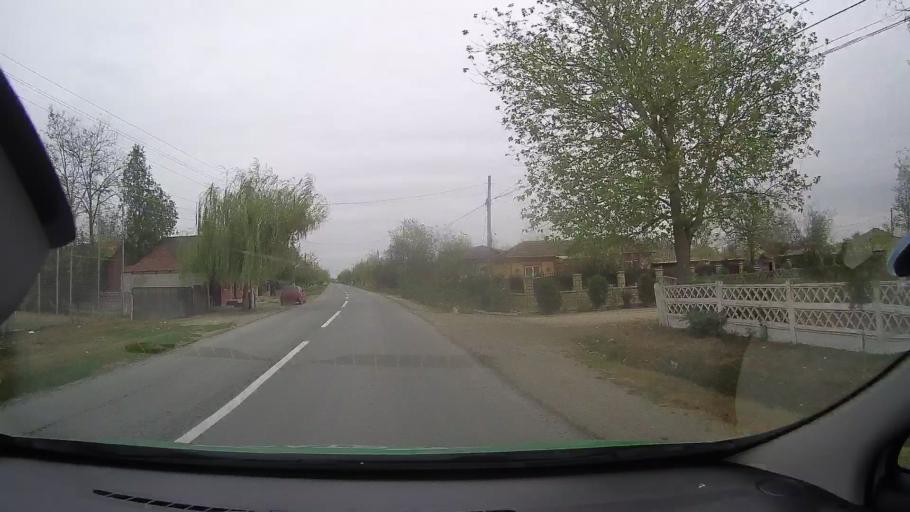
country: RO
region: Constanta
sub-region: Comuna Silistea
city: Silistea
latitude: 44.4465
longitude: 28.2390
